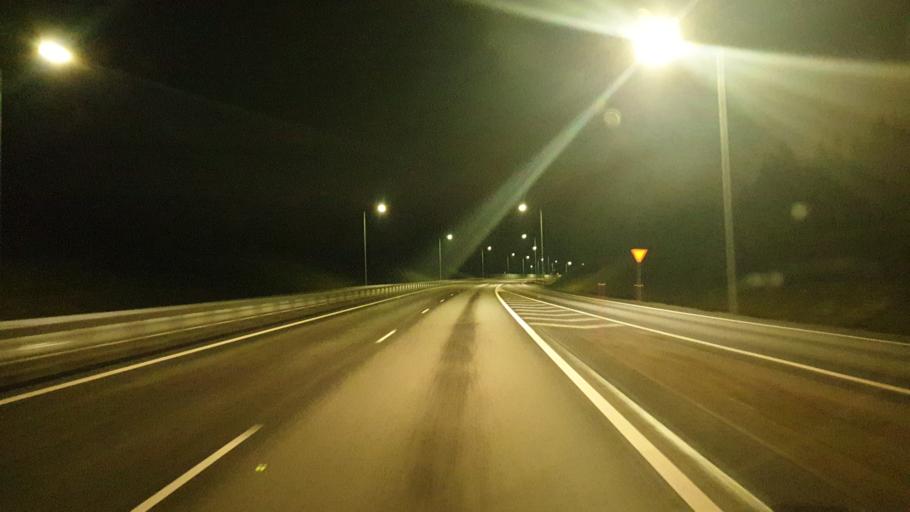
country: FI
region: Central Finland
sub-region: AEaenekoski
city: AEaenekoski
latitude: 62.5713
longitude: 25.6738
